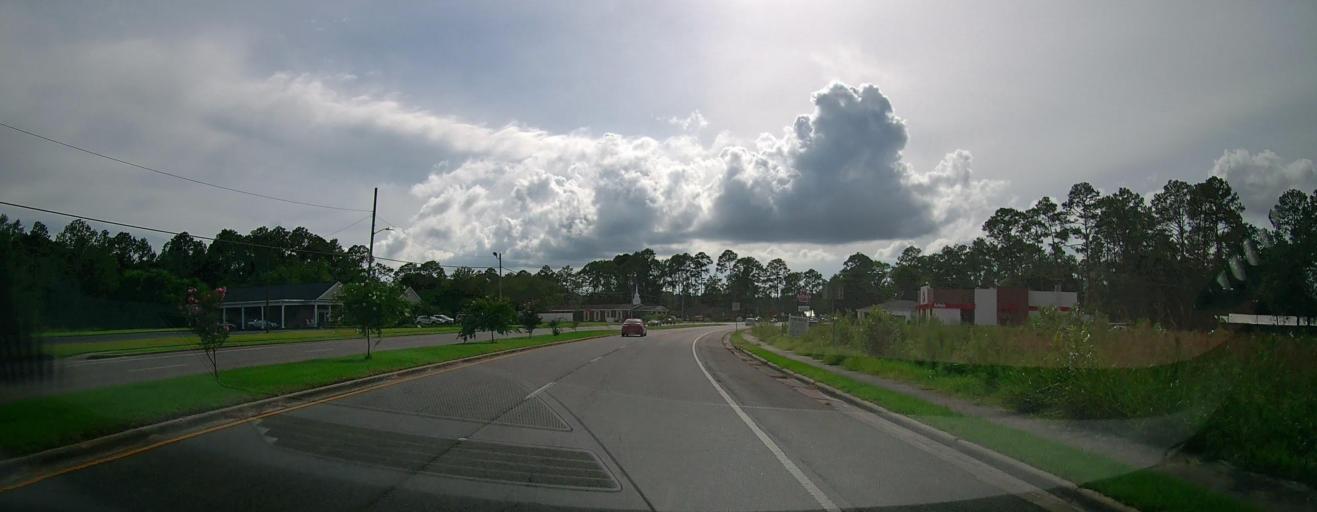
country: US
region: Georgia
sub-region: Wayne County
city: Jesup
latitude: 31.6018
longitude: -81.8934
